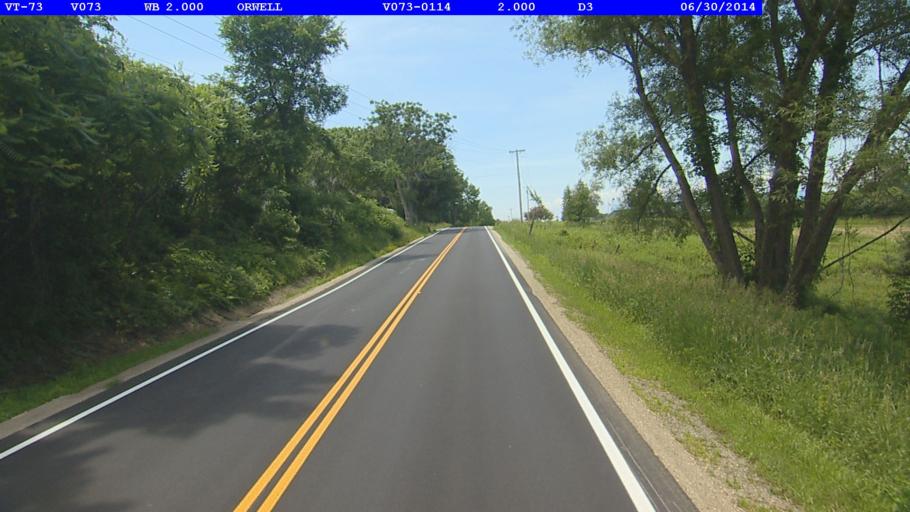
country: US
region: New York
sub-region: Essex County
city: Ticonderoga
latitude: 43.8023
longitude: -73.2661
